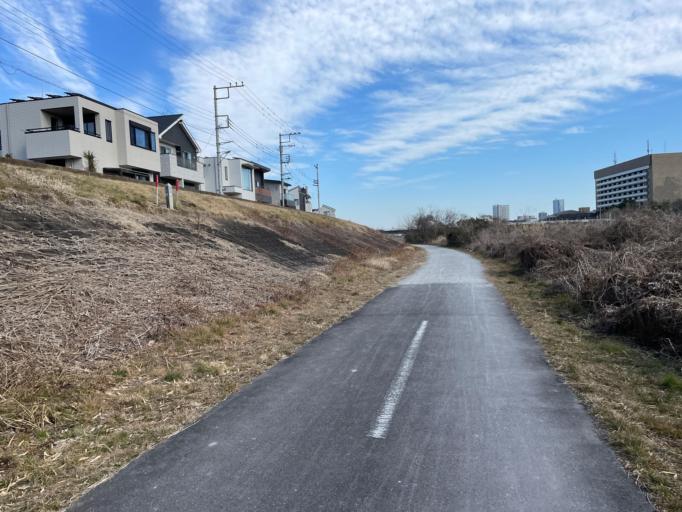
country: JP
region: Tokyo
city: Hachioji
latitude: 35.6691
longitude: 139.3129
